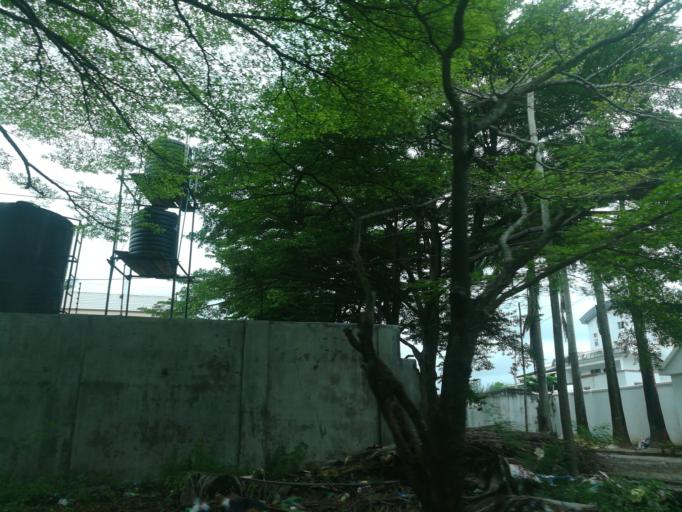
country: NG
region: Lagos
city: Ikoyi
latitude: 6.4248
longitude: 3.4211
